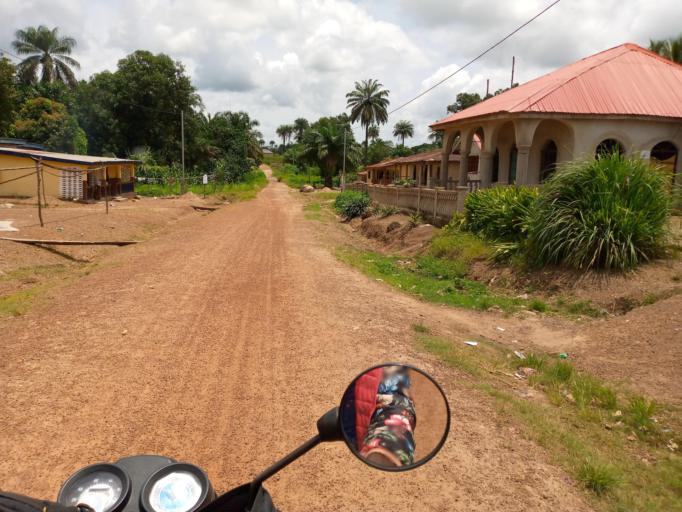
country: SL
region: Northern Province
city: Binkolo
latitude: 9.1102
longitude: -12.2012
